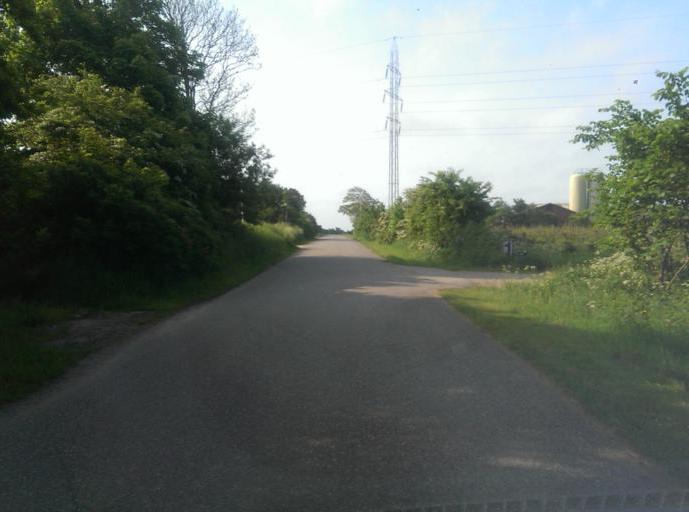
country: DK
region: South Denmark
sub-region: Esbjerg Kommune
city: Tjaereborg
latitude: 55.4473
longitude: 8.6136
